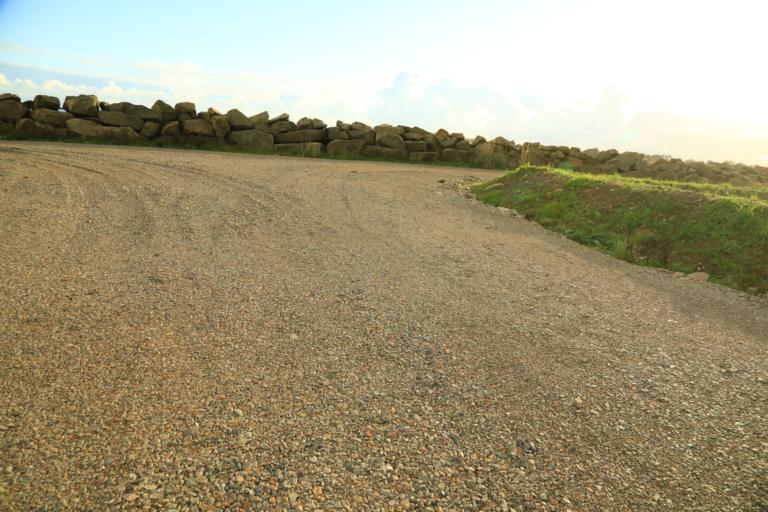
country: SE
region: Halland
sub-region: Varbergs Kommun
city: Varberg
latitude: 57.1177
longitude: 12.2384
